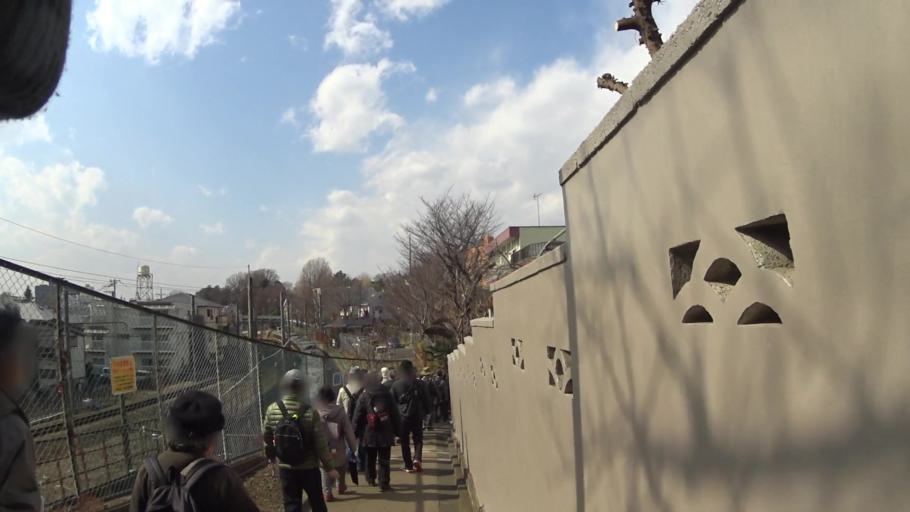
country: JP
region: Tokyo
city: Kokubunji
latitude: 35.6684
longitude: 139.4755
